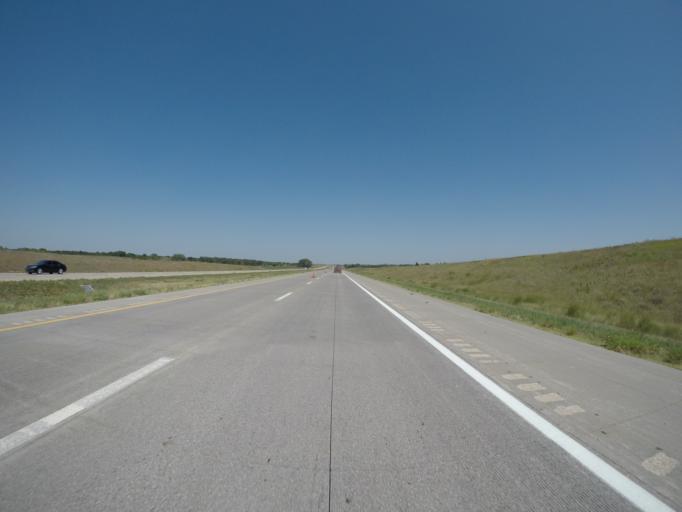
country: US
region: Kansas
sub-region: Lincoln County
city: Lincoln
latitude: 38.8782
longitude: -97.9502
